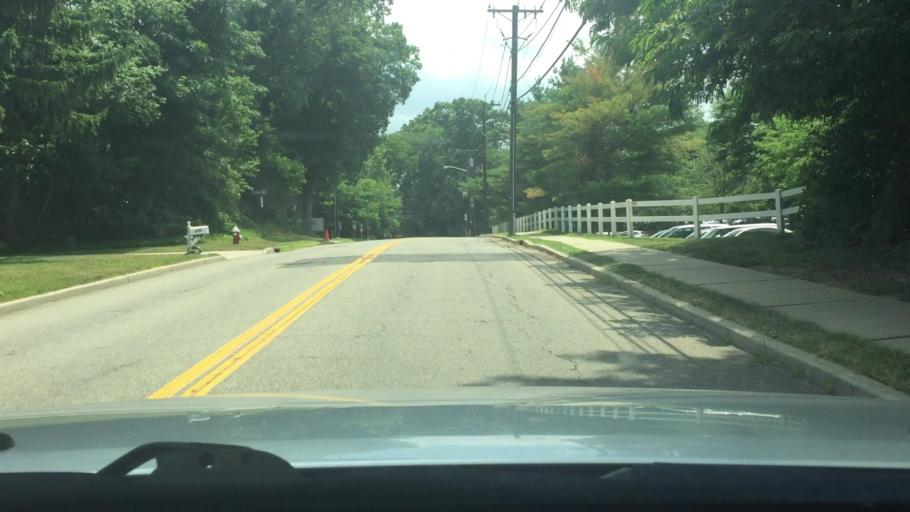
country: US
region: New Jersey
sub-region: Middlesex County
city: East Brunswick
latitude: 40.4160
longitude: -74.4109
